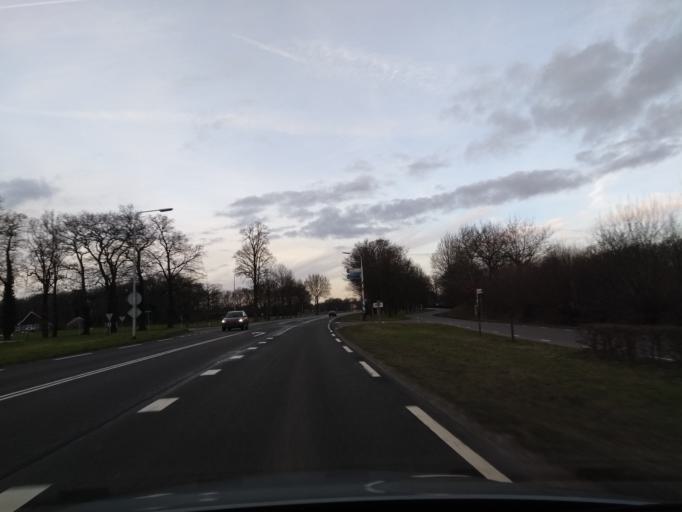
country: NL
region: Overijssel
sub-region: Gemeente Tubbergen
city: Tubbergen
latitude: 52.3578
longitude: 6.8457
